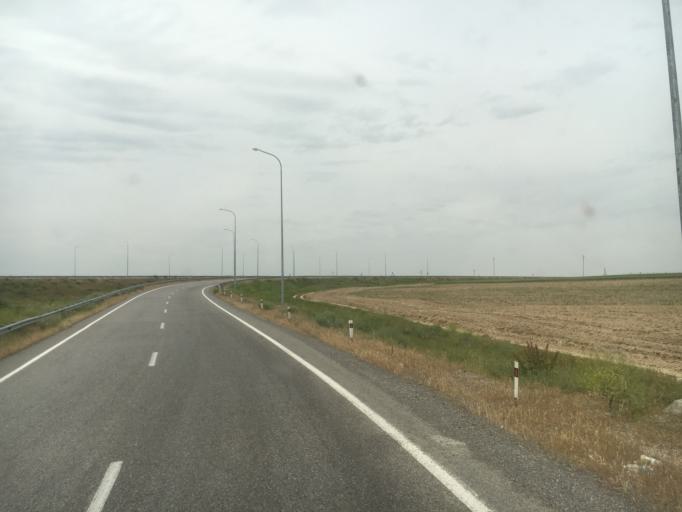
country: KZ
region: Ongtustik Qazaqstan
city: Temirlanovka
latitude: 42.5305
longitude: 69.3449
